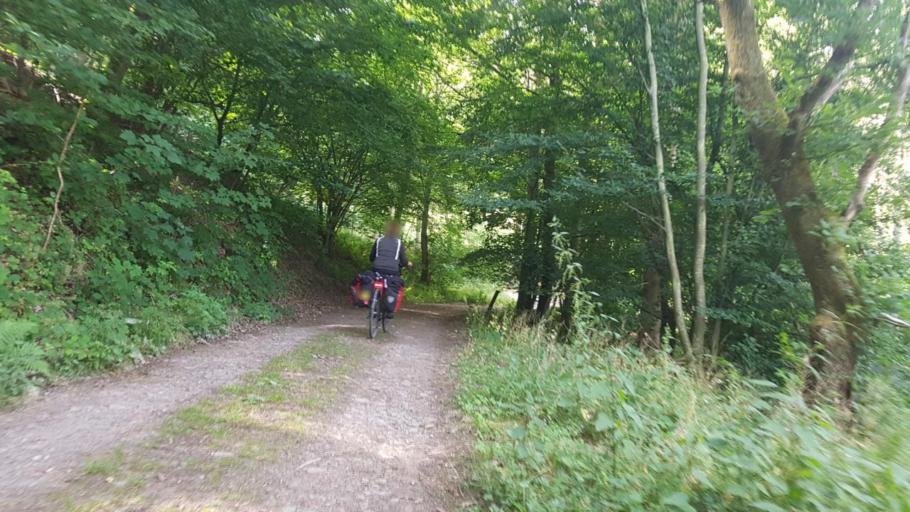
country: DE
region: North Rhine-Westphalia
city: Heimbach
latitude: 50.6209
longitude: 6.4980
